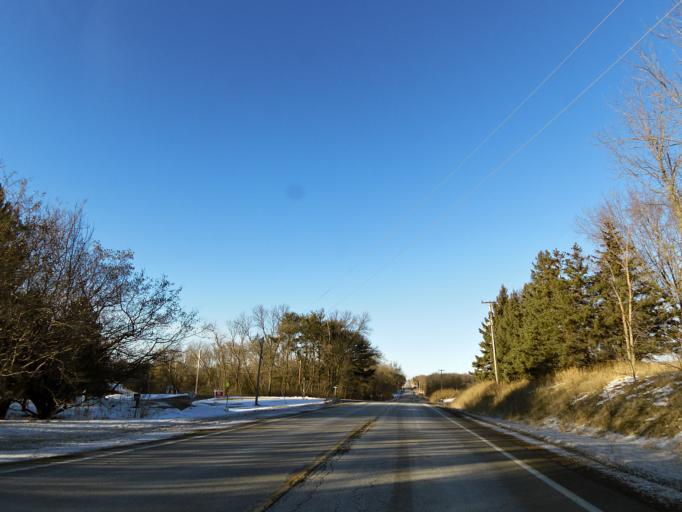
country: US
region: Minnesota
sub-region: Dakota County
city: Hastings
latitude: 44.7928
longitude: -92.8629
